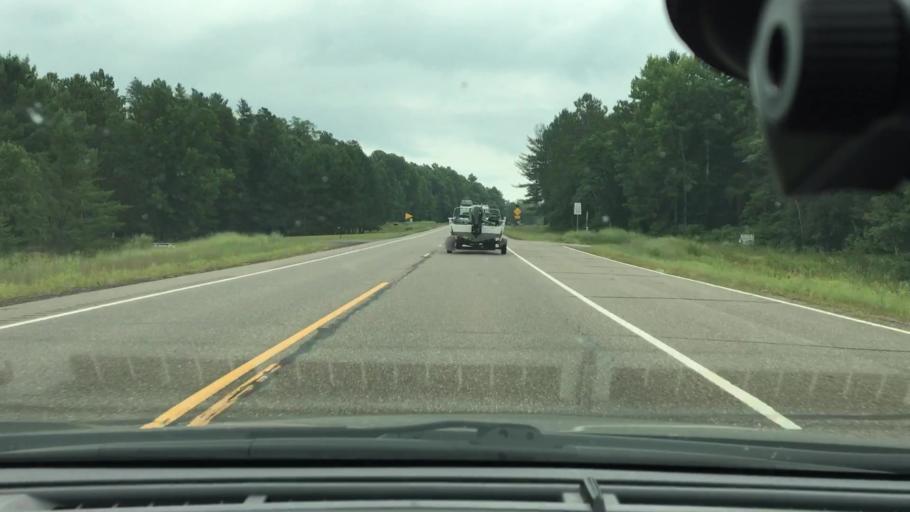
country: US
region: Minnesota
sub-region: Crow Wing County
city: Crosby
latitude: 46.5435
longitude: -93.9550
